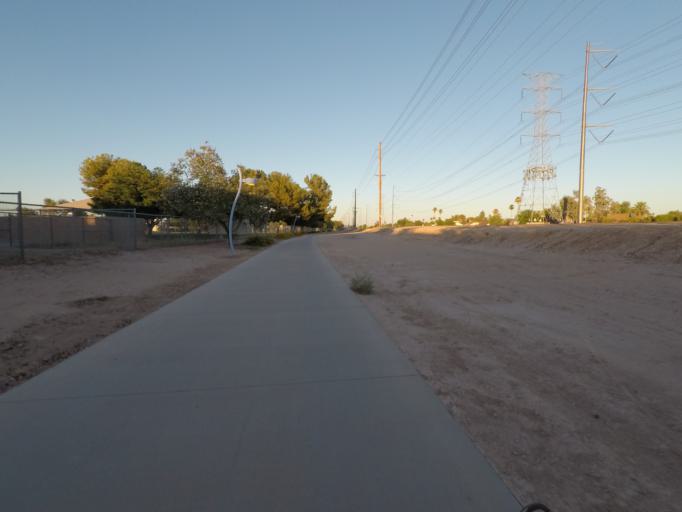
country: US
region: Arizona
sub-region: Maricopa County
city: Guadalupe
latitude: 33.3566
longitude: -111.9176
